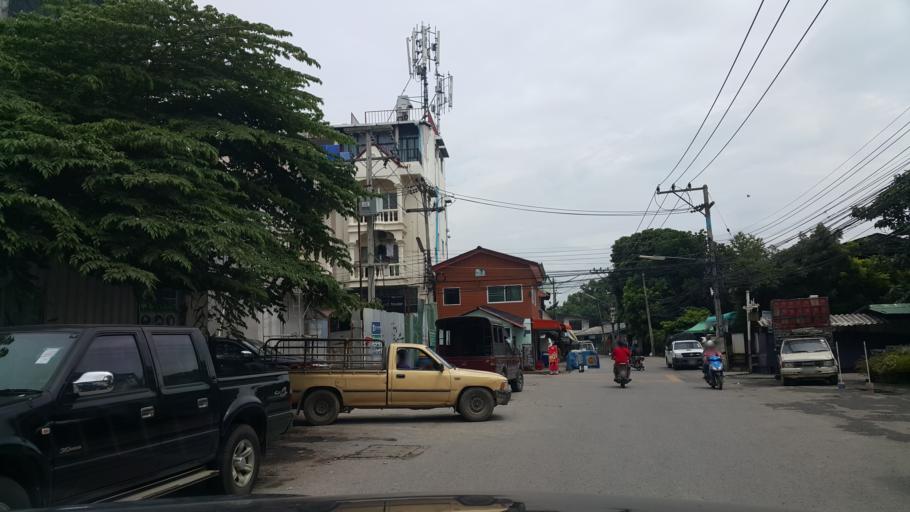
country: TH
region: Chiang Mai
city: Chiang Mai
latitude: 18.7916
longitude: 98.9962
